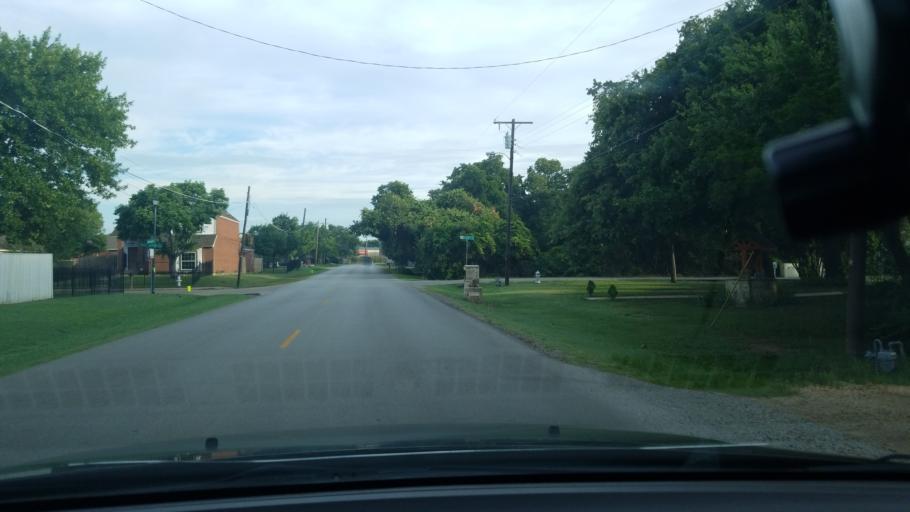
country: US
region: Texas
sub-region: Dallas County
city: Balch Springs
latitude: 32.7578
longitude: -96.6417
